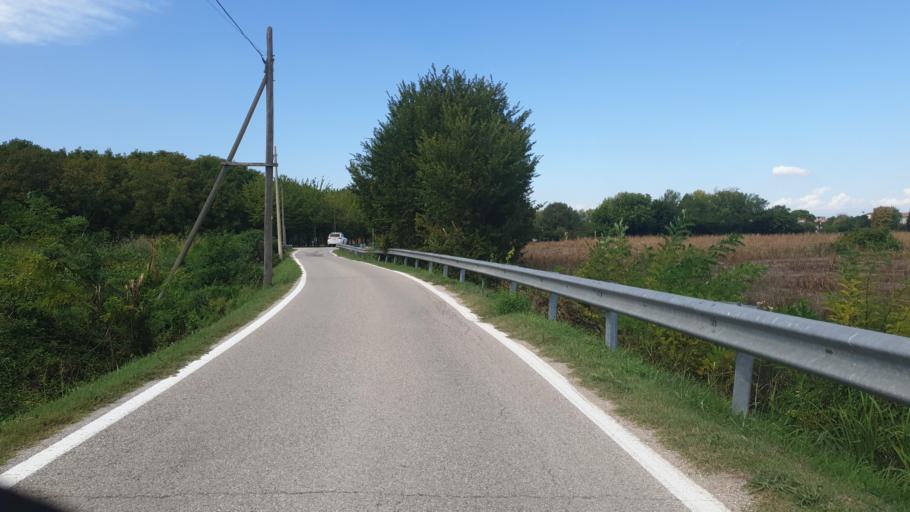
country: IT
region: Veneto
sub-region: Provincia di Padova
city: Terradura
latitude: 45.3334
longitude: 11.8152
